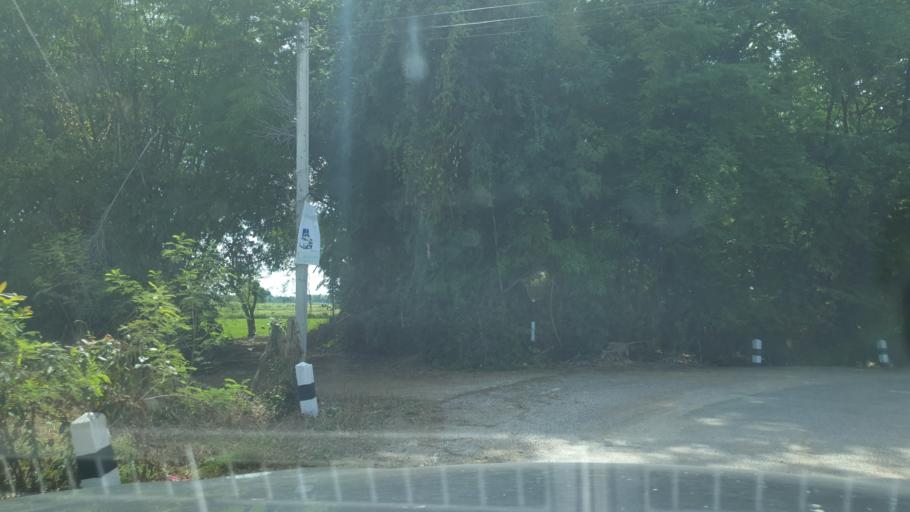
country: TH
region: Sukhothai
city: Si Samrong
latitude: 17.2027
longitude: 99.7211
